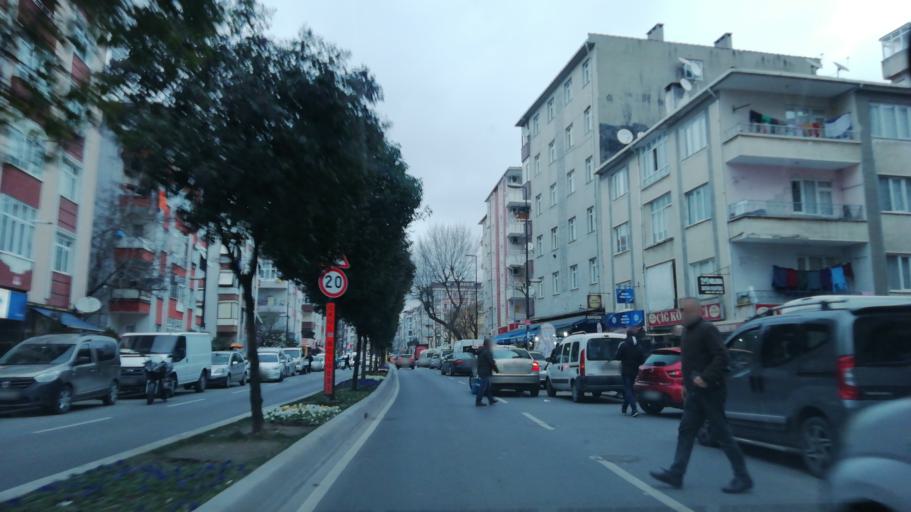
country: TR
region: Istanbul
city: Bahcelievler
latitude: 41.0084
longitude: 28.8498
